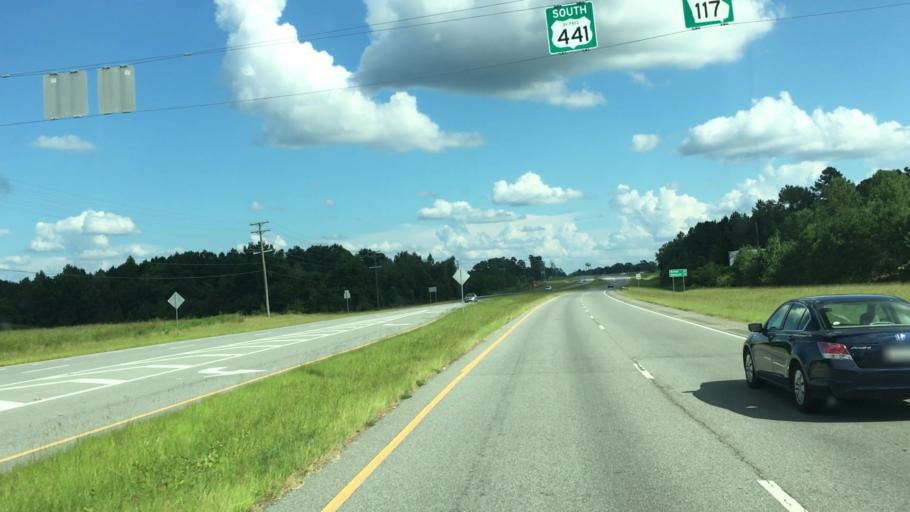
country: US
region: Georgia
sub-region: Laurens County
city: Dublin
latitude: 32.5150
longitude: -82.9552
